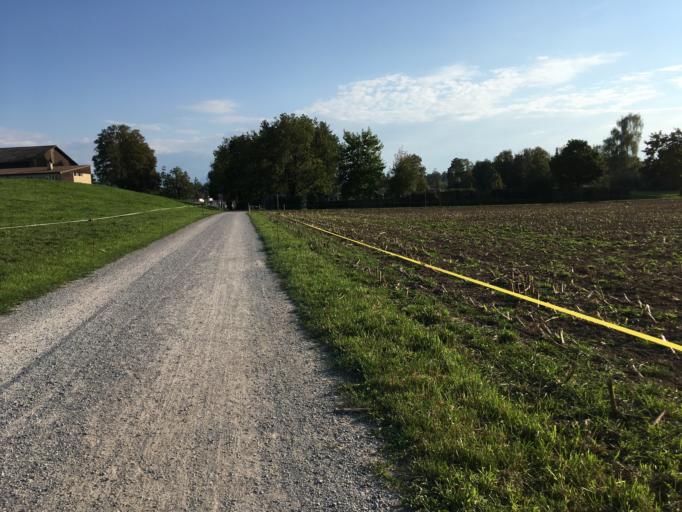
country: CH
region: Zurich
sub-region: Bezirk Hinwil
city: Wetzikon / Ober-Wetzikon
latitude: 47.3182
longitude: 8.8011
